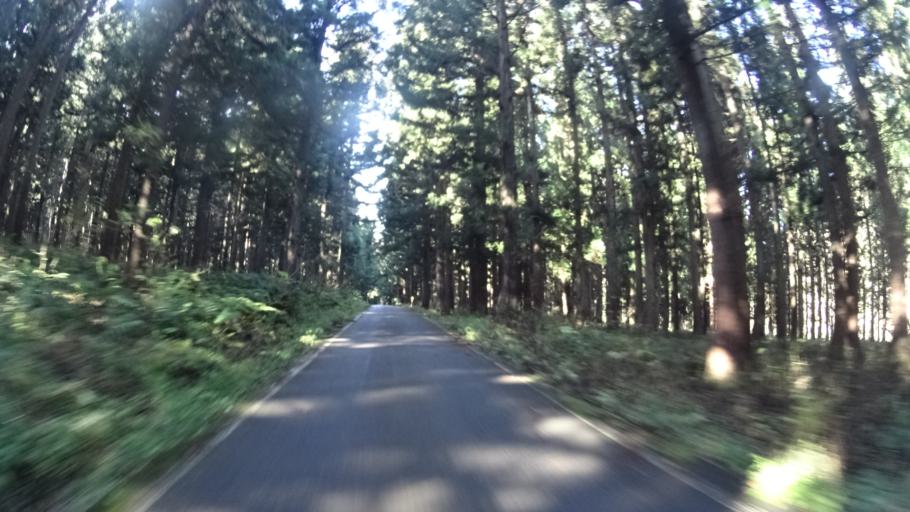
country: JP
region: Niigata
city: Muikamachi
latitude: 37.1793
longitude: 139.0844
